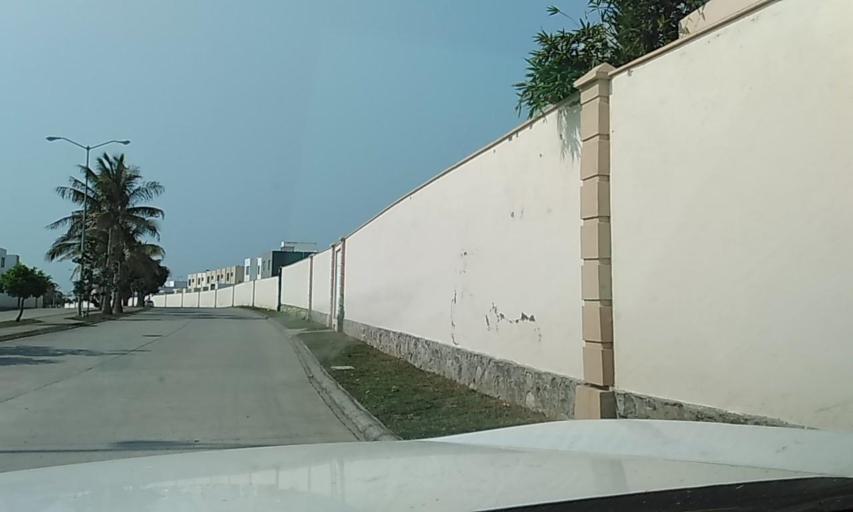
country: MX
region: Veracruz
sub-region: Alvarado
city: Playa de la Libertad
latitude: 19.0463
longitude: -96.0607
